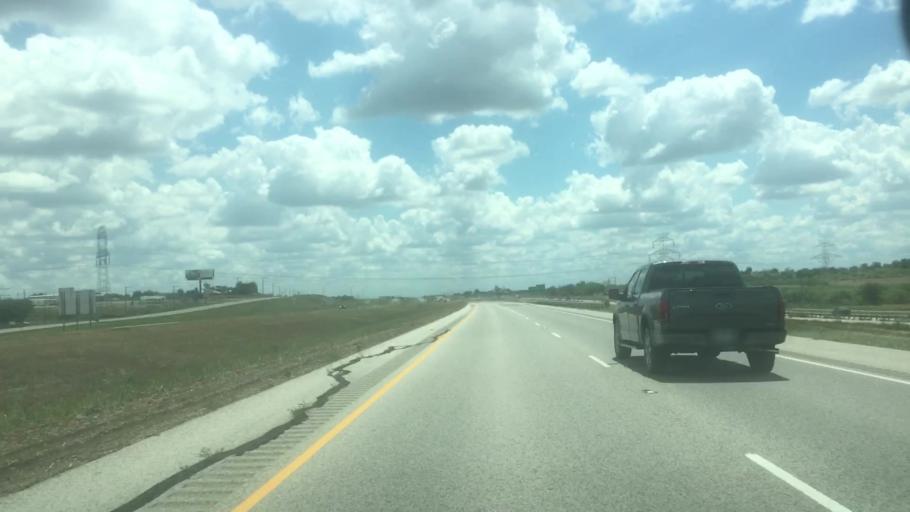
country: US
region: Texas
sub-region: Caldwell County
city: Uhland
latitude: 29.9989
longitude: -97.6865
